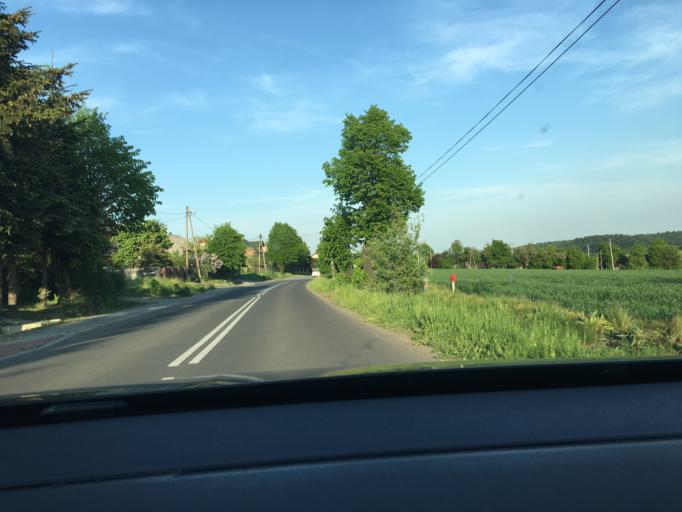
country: PL
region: Lesser Poland Voivodeship
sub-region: Powiat krakowski
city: Saspow
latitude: 50.2310
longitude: 19.7845
